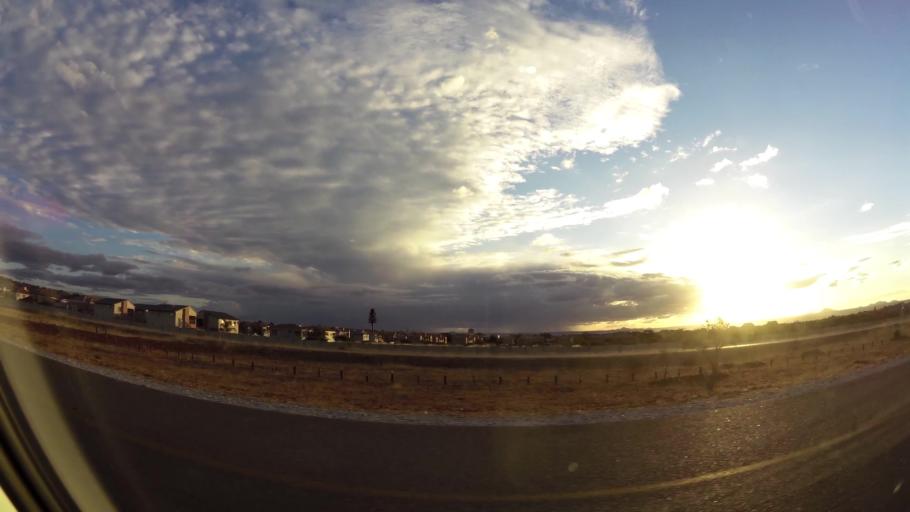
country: ZA
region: Limpopo
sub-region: Capricorn District Municipality
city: Polokwane
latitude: -23.8816
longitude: 29.5080
